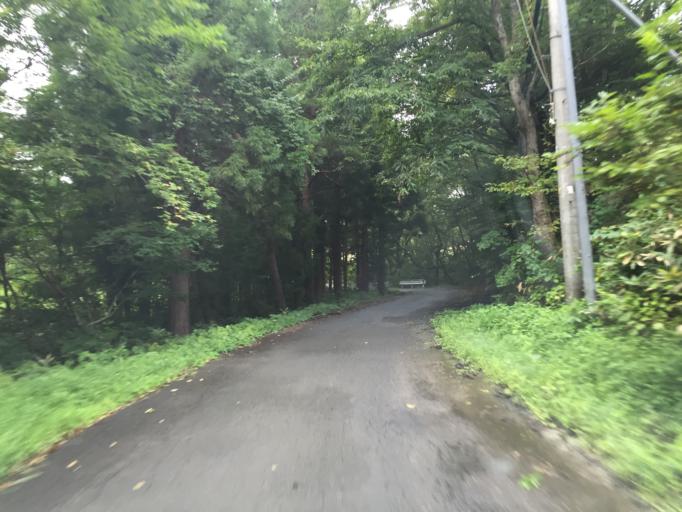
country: JP
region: Fukushima
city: Fukushima-shi
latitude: 37.8132
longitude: 140.3444
